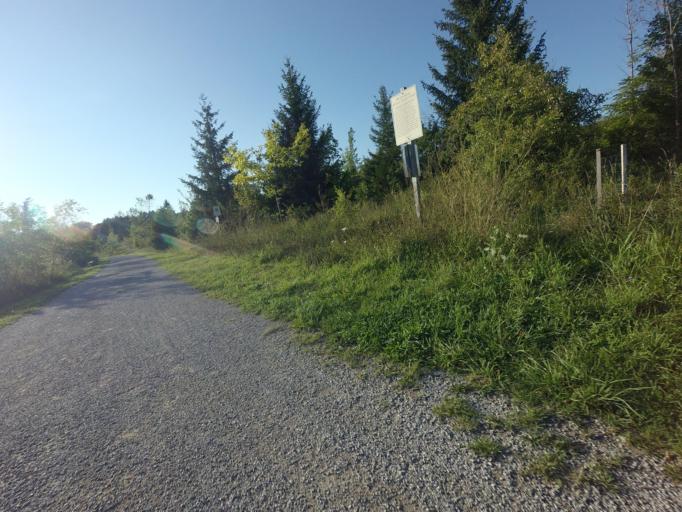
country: CA
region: Ontario
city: Goderich
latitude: 43.7597
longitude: -81.7050
